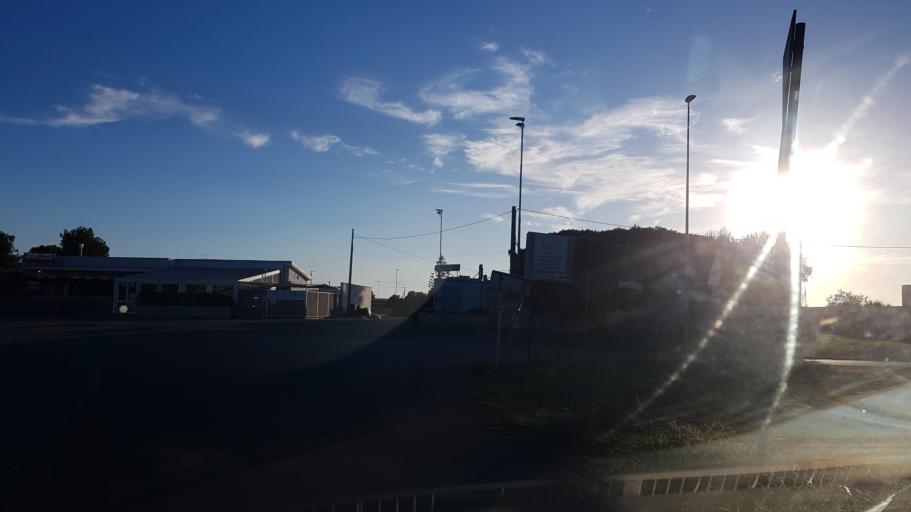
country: IT
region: Apulia
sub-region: Provincia di Lecce
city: Merine
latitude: 40.4264
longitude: 18.2398
